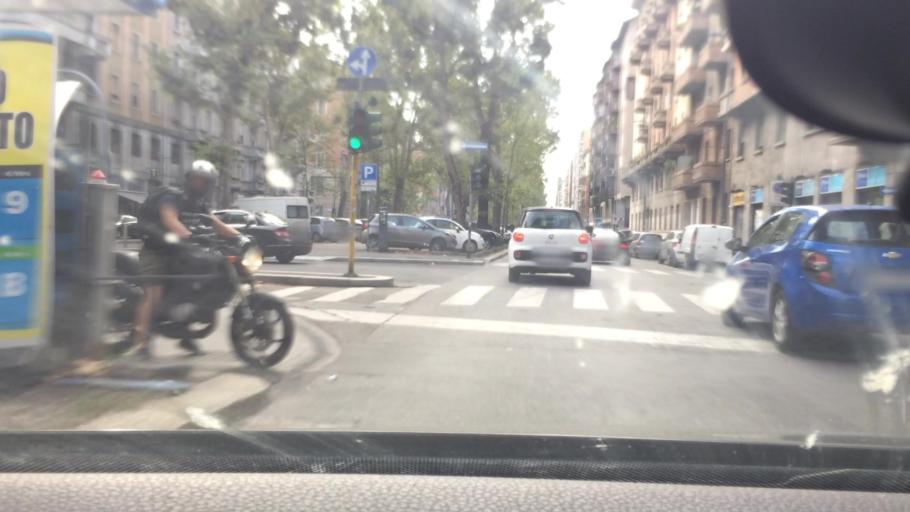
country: IT
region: Lombardy
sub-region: Citta metropolitana di Milano
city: Milano
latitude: 45.4889
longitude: 9.2102
